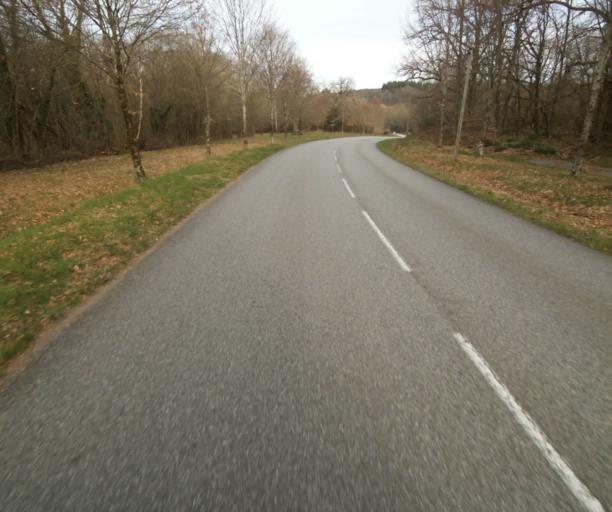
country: FR
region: Limousin
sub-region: Departement de la Correze
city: Treignac
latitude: 45.4437
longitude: 1.8086
